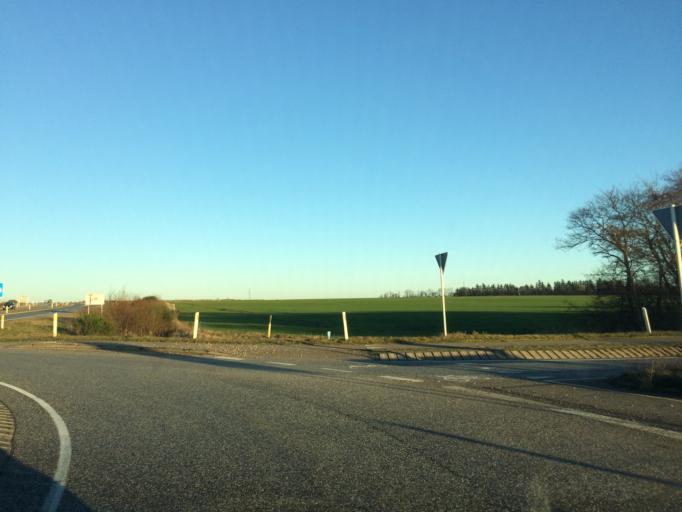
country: DK
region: Central Jutland
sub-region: Herning Kommune
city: Snejbjerg
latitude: 56.1873
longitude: 8.8955
